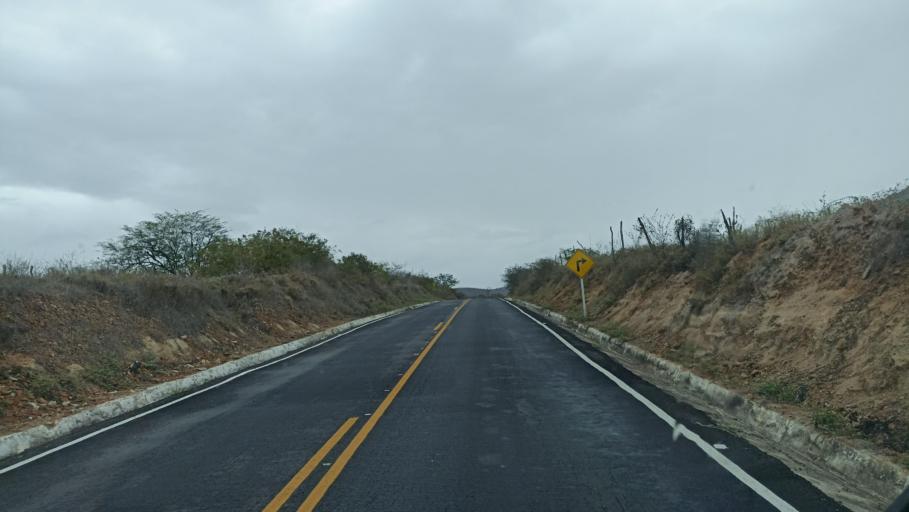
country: BR
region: Bahia
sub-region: Andarai
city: Vera Cruz
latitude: -13.0492
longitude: -40.7522
